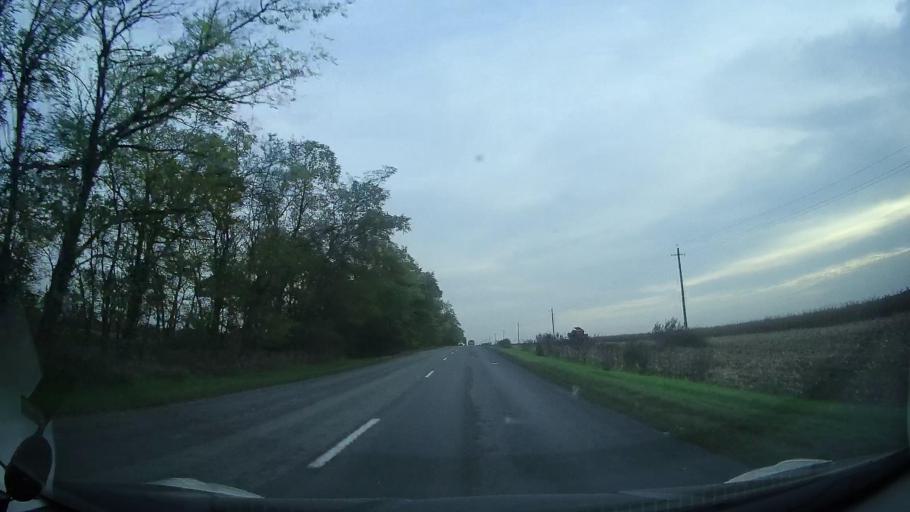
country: RU
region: Rostov
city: Ol'ginskaya
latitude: 47.0984
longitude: 39.9776
